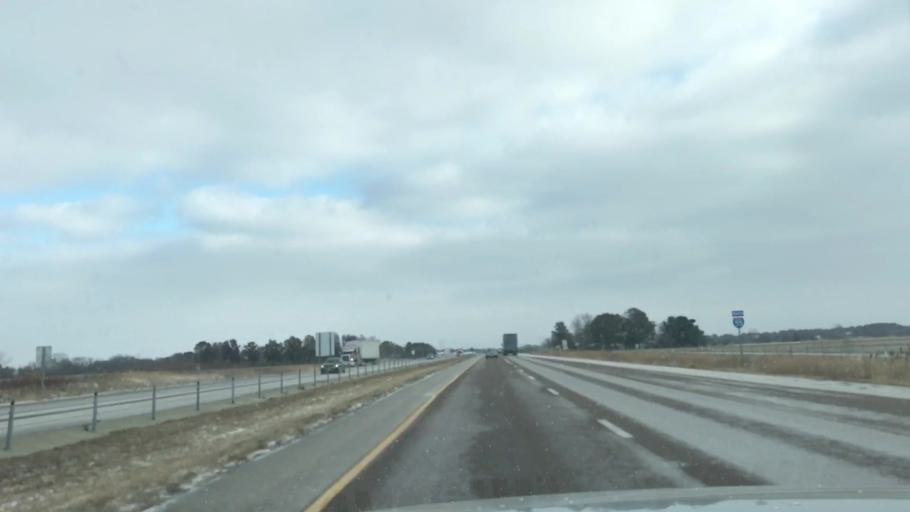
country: US
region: Illinois
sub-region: Madison County
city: Worden
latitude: 38.9341
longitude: -89.7982
